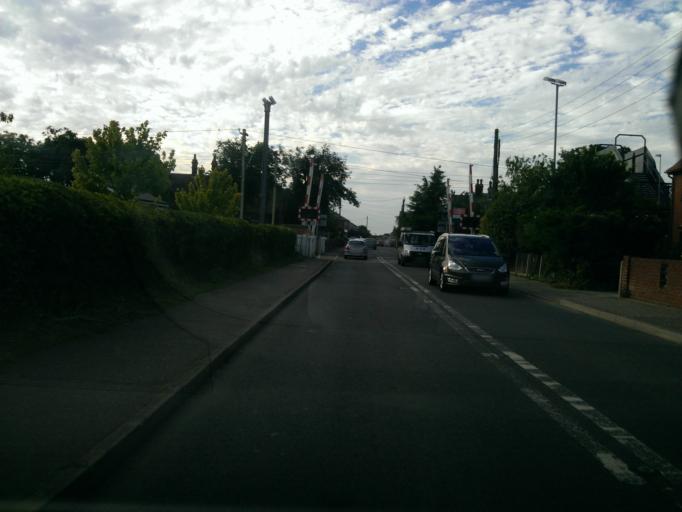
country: GB
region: England
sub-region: Essex
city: Great Bentley
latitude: 51.8512
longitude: 1.0650
